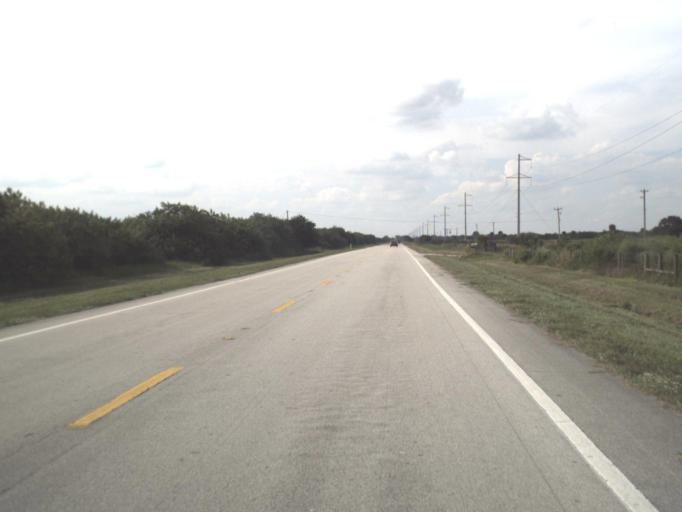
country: US
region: Florida
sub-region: Okeechobee County
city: Taylor Creek
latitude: 27.1844
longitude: -80.7156
